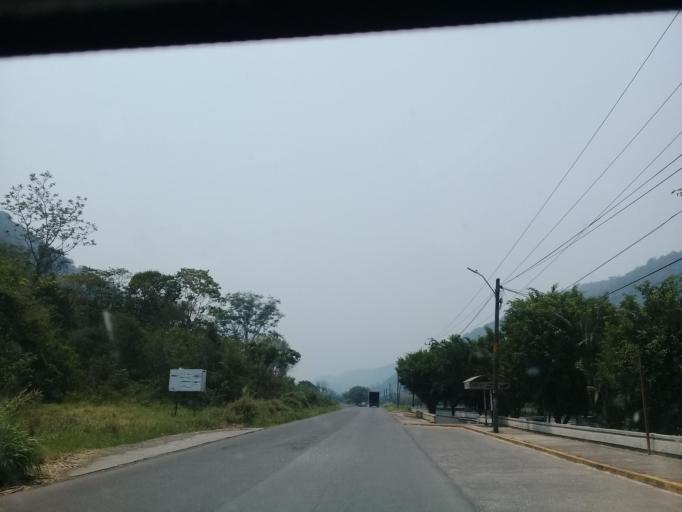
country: MX
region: Veracruz
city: Tezonapa
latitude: 18.6154
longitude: -96.6961
